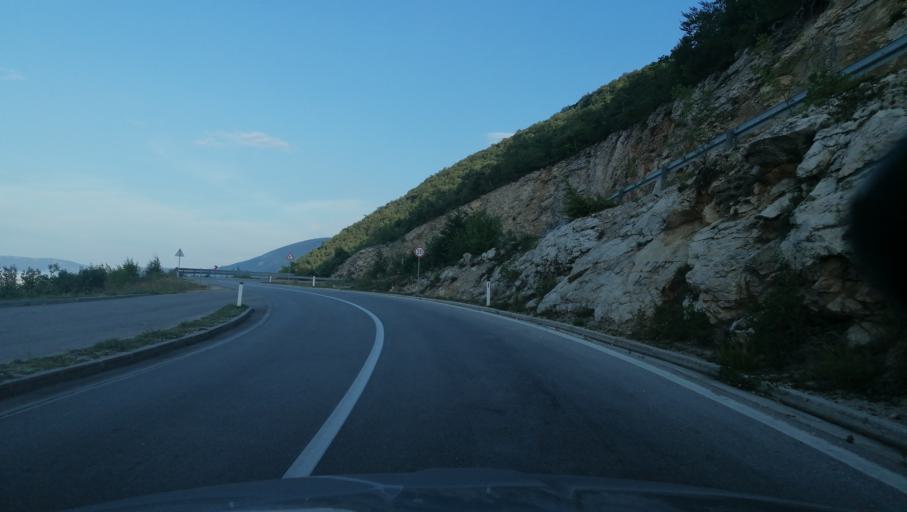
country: BA
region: Federation of Bosnia and Herzegovina
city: Prozor
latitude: 43.8387
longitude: 17.5820
